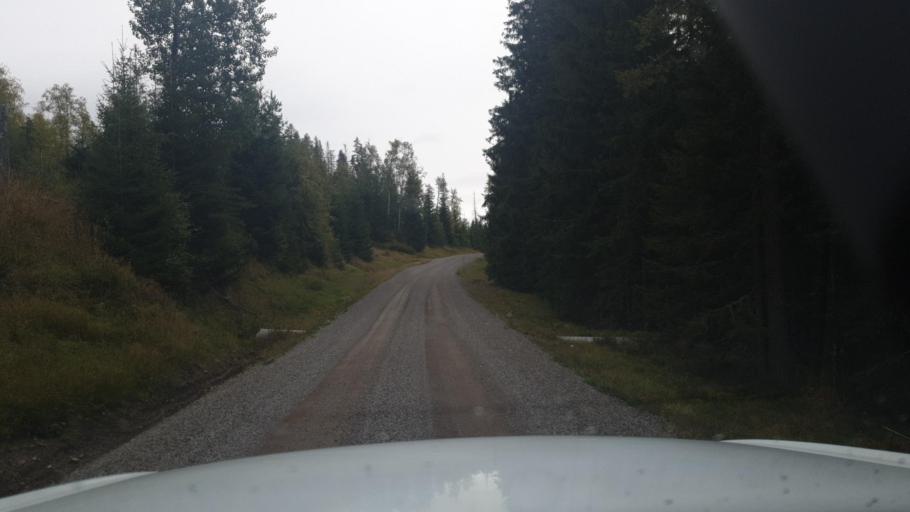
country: SE
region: Vaermland
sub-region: Eda Kommun
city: Charlottenberg
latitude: 60.0910
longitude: 12.6160
